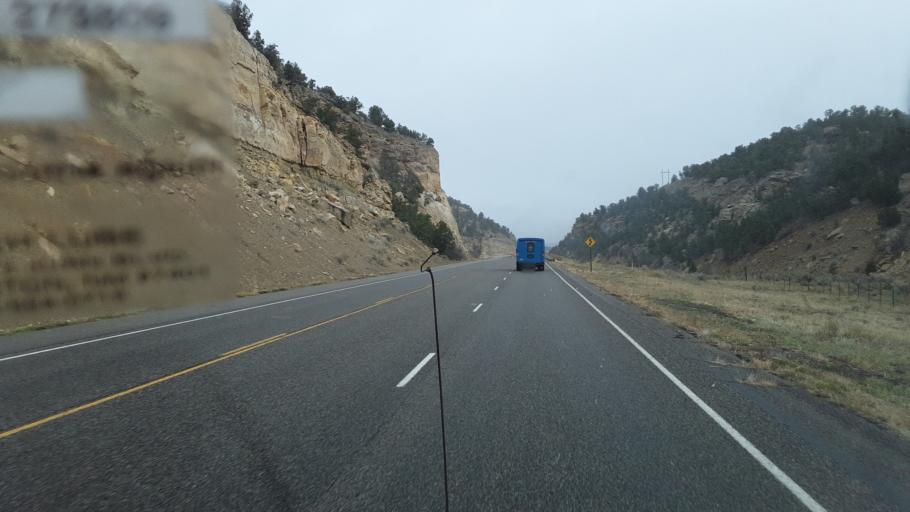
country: US
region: New Mexico
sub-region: Rio Arriba County
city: Tierra Amarilla
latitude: 36.4182
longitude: -106.4810
